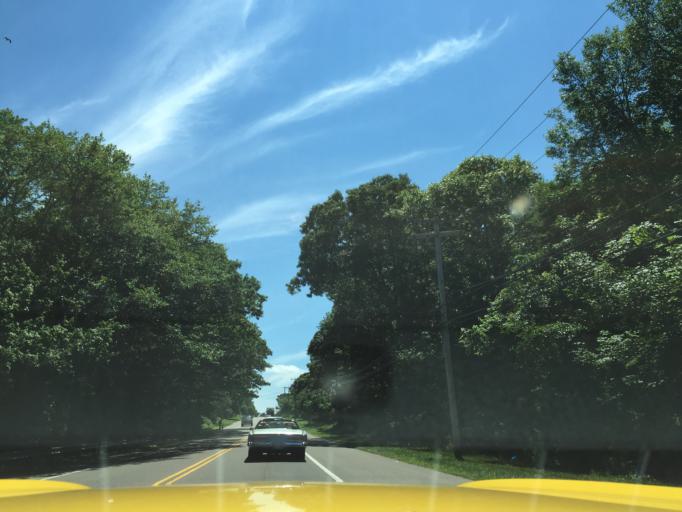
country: US
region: New York
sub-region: Suffolk County
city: Montauk
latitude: 41.0663
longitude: -71.9472
